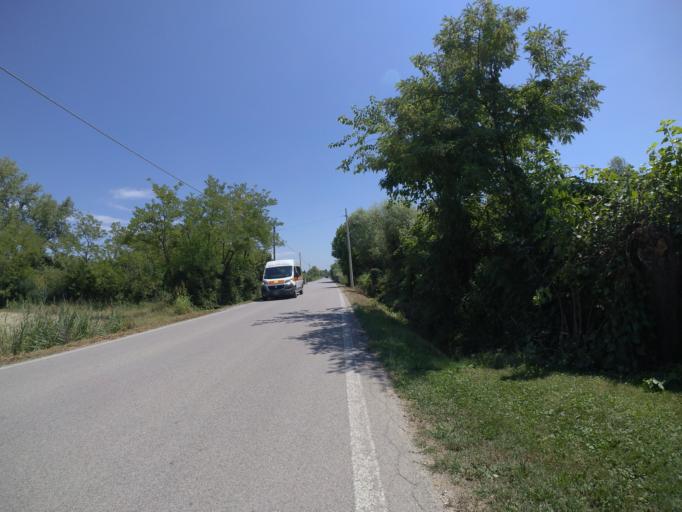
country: IT
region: Friuli Venezia Giulia
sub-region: Provincia di Udine
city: Pocenia
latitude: 45.8683
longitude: 13.1041
